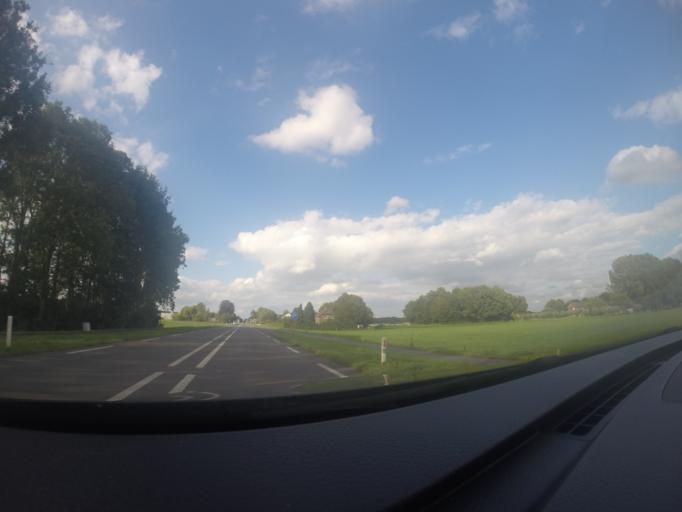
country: NL
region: Gelderland
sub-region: Gemeente Bronckhorst
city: Baak
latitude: 52.0649
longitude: 6.2238
